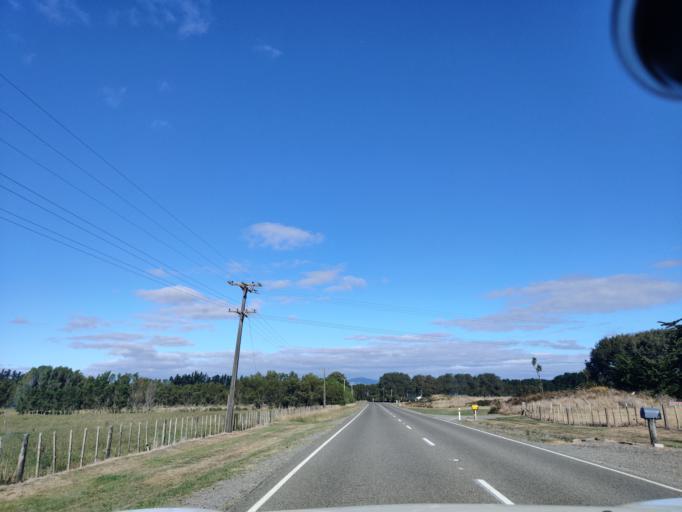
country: NZ
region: Manawatu-Wanganui
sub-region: Horowhenua District
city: Foxton
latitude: -40.4180
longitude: 175.4082
